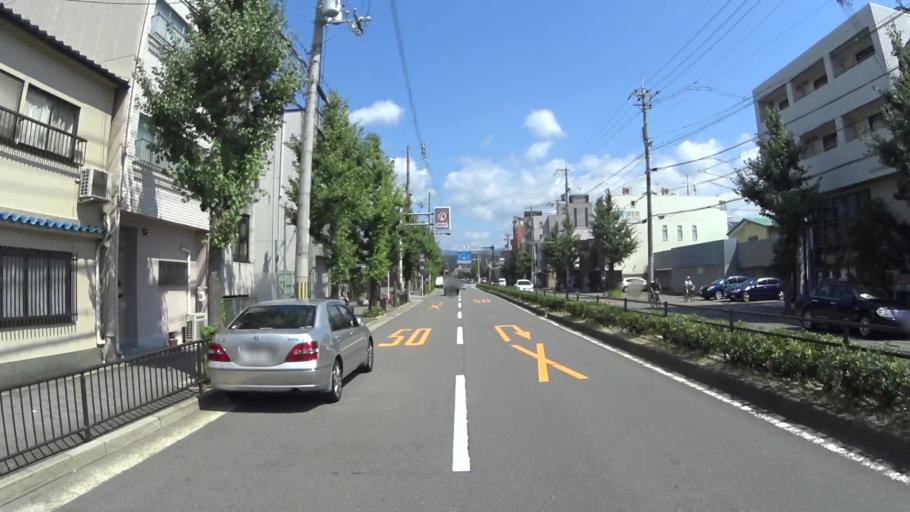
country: JP
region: Kyoto
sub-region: Kyoto-shi
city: Kamigyo-ku
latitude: 35.0421
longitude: 135.7708
